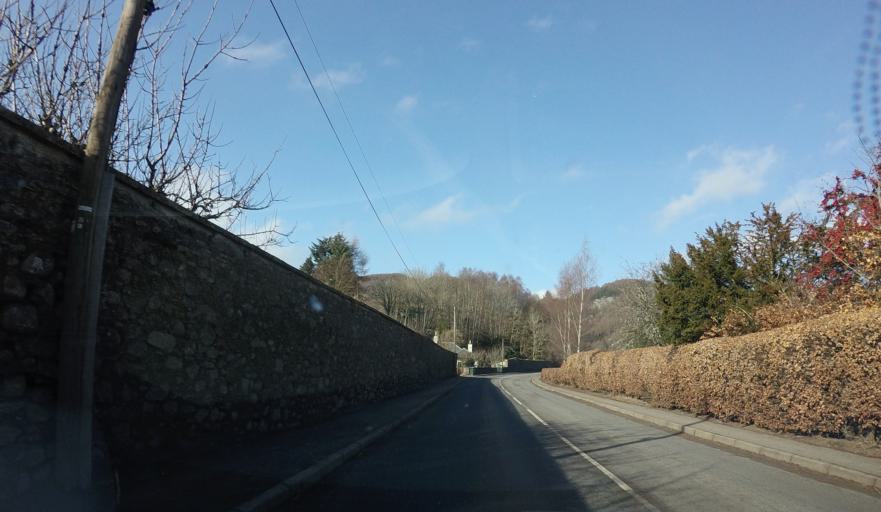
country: GB
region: Scotland
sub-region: Perth and Kinross
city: Bankfoot
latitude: 56.5687
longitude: -3.5878
